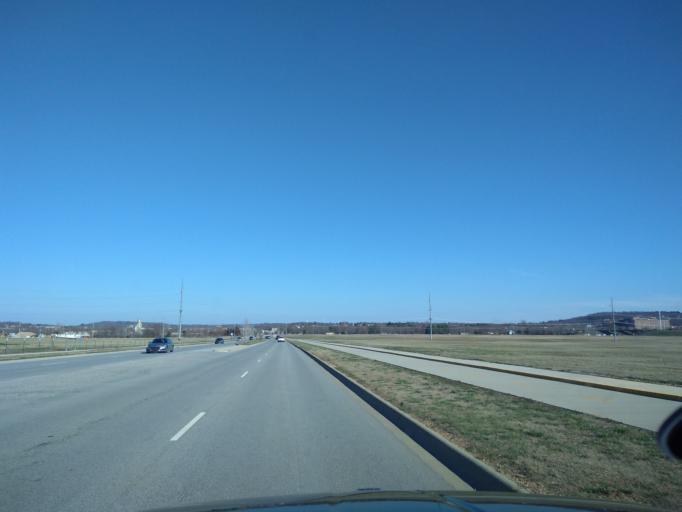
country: US
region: Arkansas
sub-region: Washington County
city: Johnson
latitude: 36.1171
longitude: -94.1724
